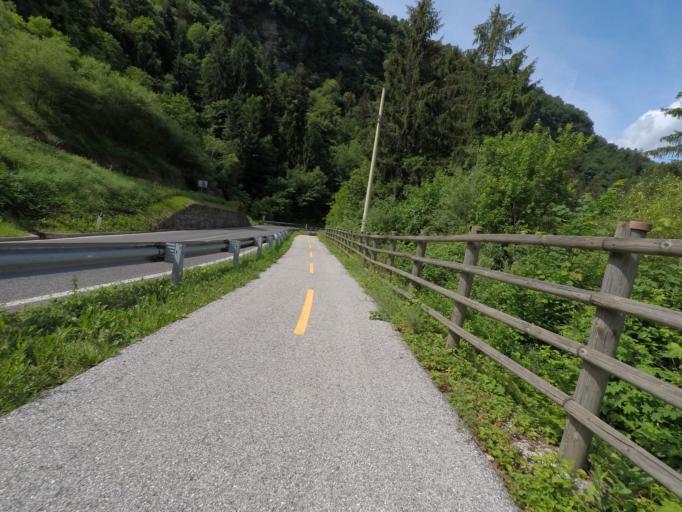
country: IT
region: Friuli Venezia Giulia
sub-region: Provincia di Udine
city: Tolmezzo
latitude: 46.3813
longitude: 13.0208
